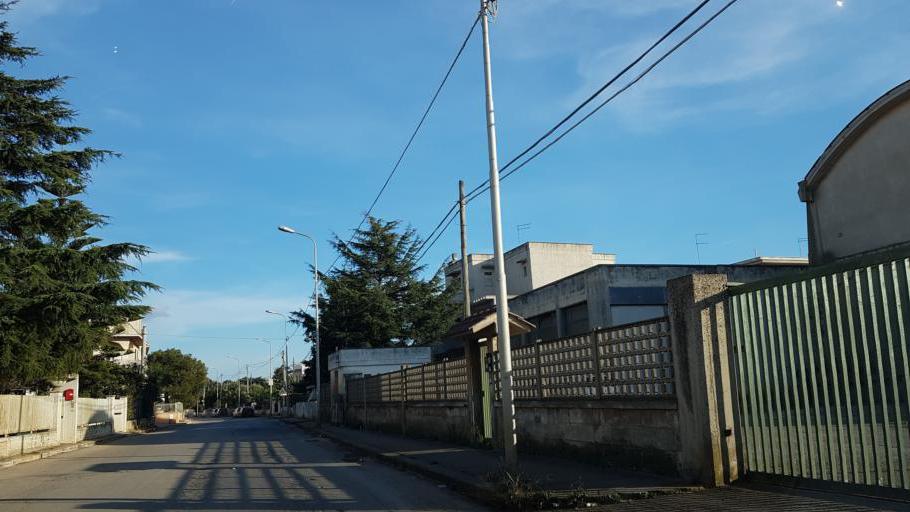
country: IT
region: Apulia
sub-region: Provincia di Brindisi
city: Carovigno
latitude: 40.7029
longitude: 17.6665
